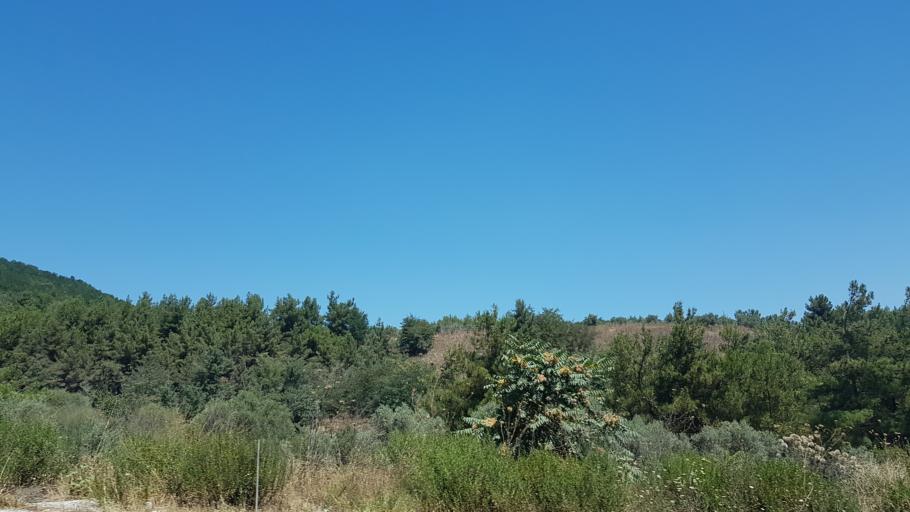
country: TR
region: Mugla
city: Yatagan
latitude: 37.3188
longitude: 28.0793
